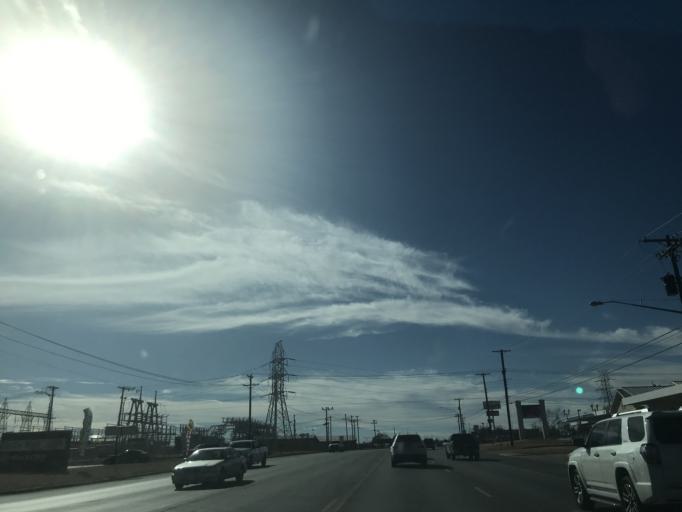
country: US
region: Texas
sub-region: Erath County
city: Stephenville
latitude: 32.2067
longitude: -98.2320
